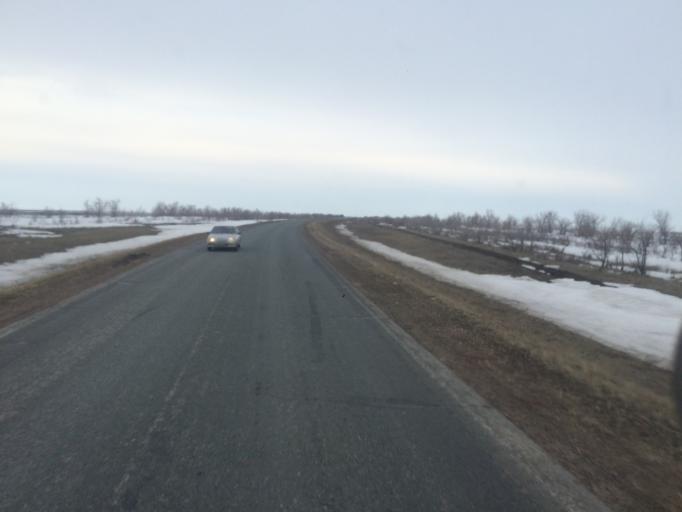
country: KZ
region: Batys Qazaqstan
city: Oral
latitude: 51.4338
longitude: 51.2649
